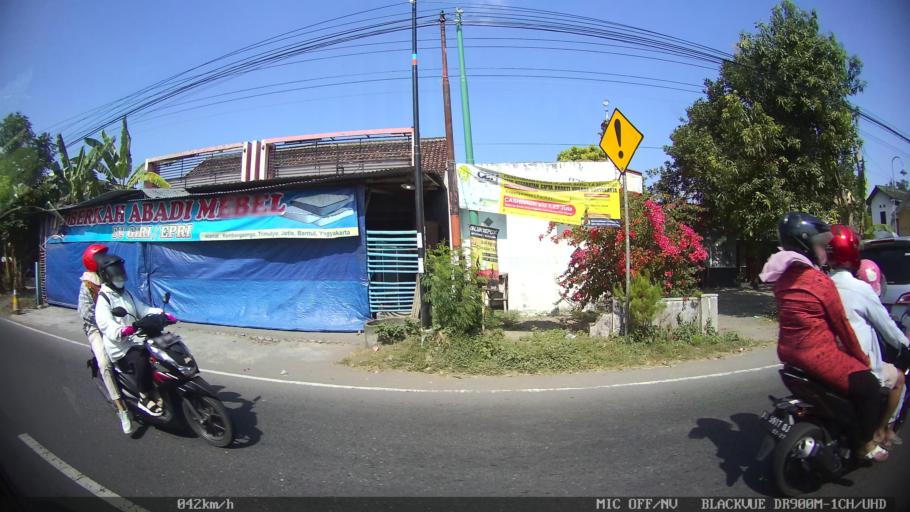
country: ID
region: Daerah Istimewa Yogyakarta
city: Sewon
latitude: -7.8904
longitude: 110.3864
